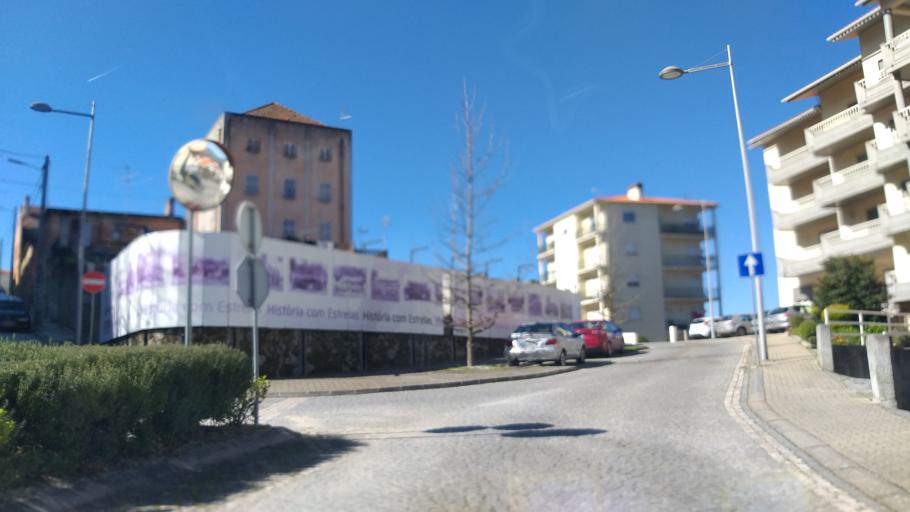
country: PT
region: Guarda
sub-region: Manteigas
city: Manteigas
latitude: 40.4979
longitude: -7.5887
